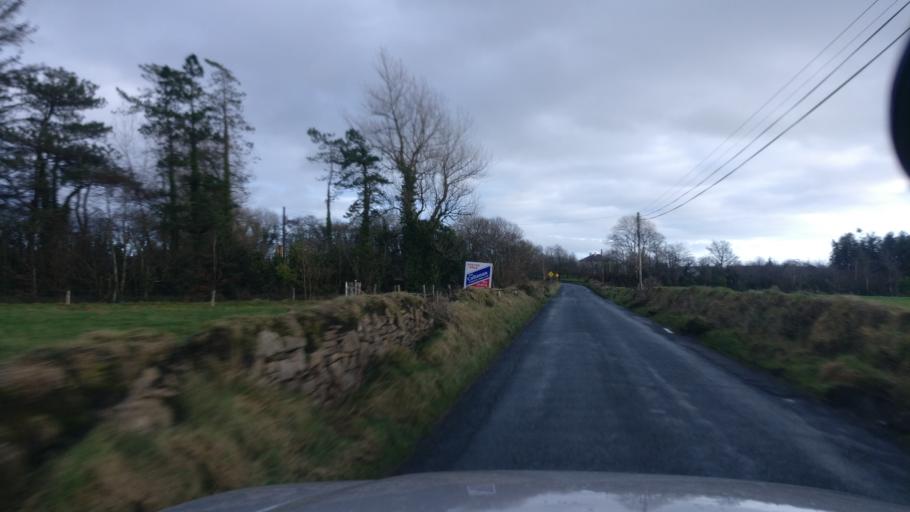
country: IE
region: Connaught
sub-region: County Galway
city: Athenry
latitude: 53.2962
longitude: -8.6995
